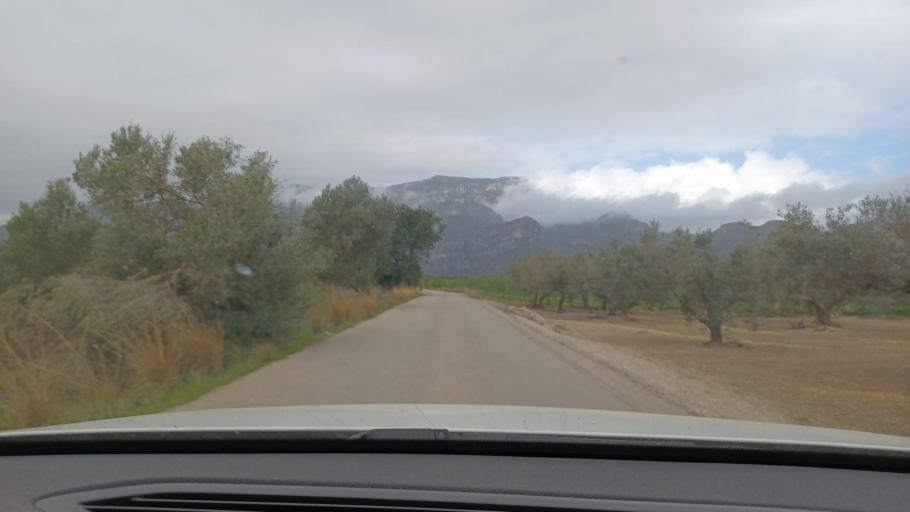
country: ES
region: Catalonia
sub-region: Provincia de Tarragona
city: Mas de Barberans
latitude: 40.7971
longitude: 0.4306
